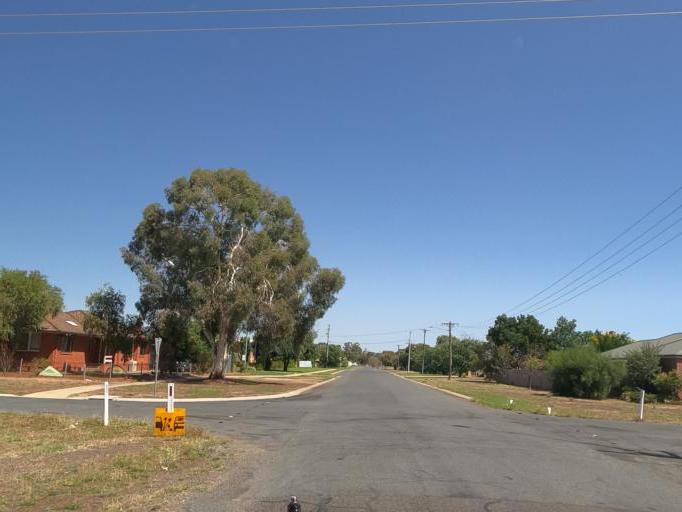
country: AU
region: New South Wales
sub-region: Corowa Shire
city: Mulwala
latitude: -35.9865
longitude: 146.0046
